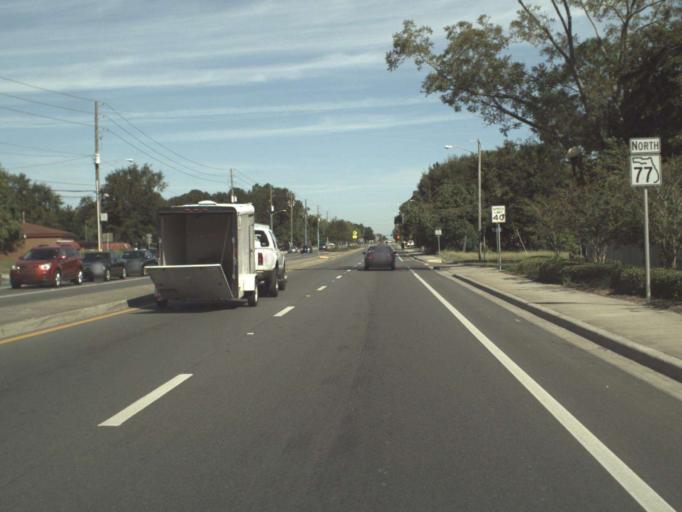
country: US
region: Florida
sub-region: Bay County
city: Panama City
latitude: 30.1681
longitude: -85.6502
